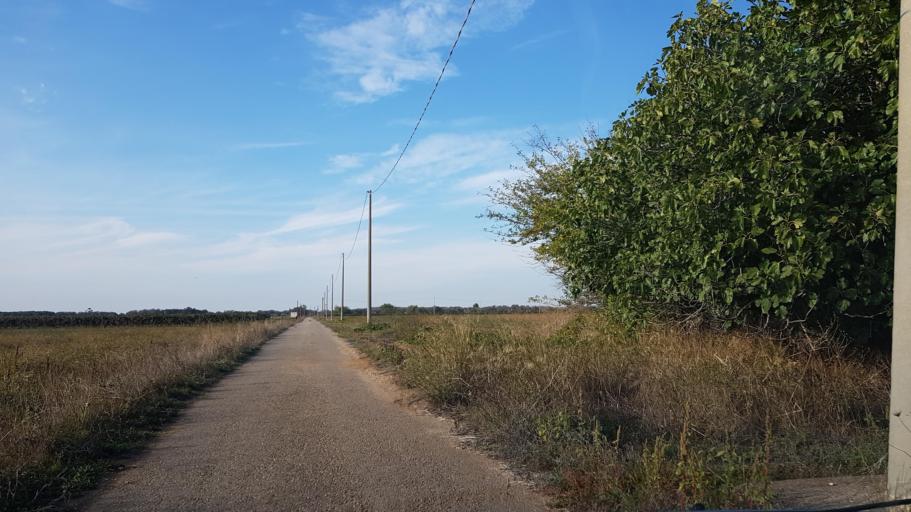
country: IT
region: Apulia
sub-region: Provincia di Brindisi
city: Mesagne
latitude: 40.4971
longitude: 17.8520
